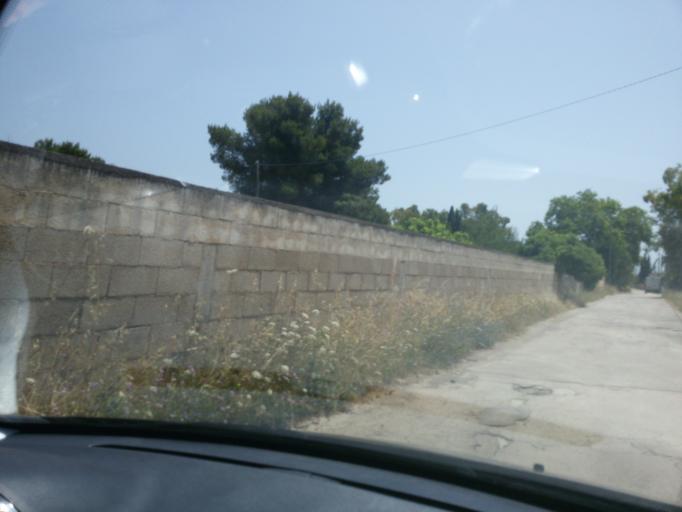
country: IT
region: Apulia
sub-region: Provincia di Lecce
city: Porto Cesareo
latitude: 40.2498
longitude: 17.9220
